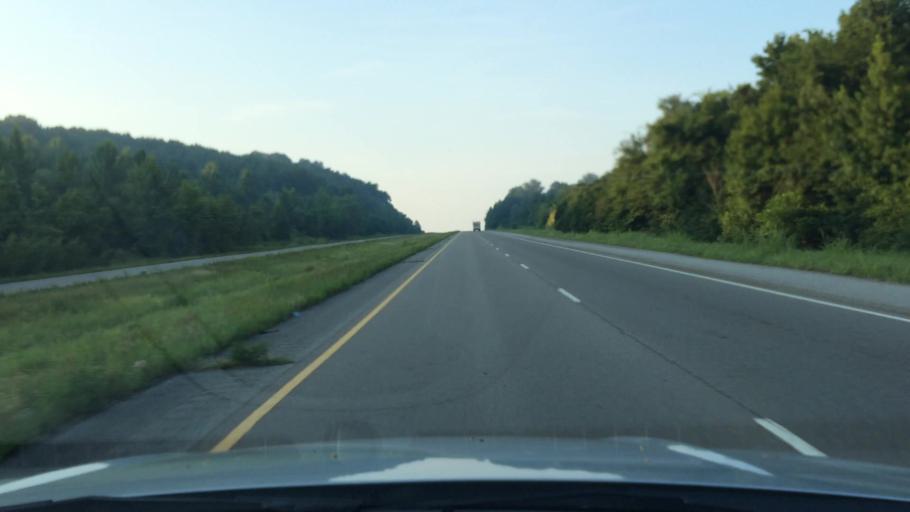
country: US
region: Tennessee
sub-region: Giles County
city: Pulaski
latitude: 35.1839
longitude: -87.0628
